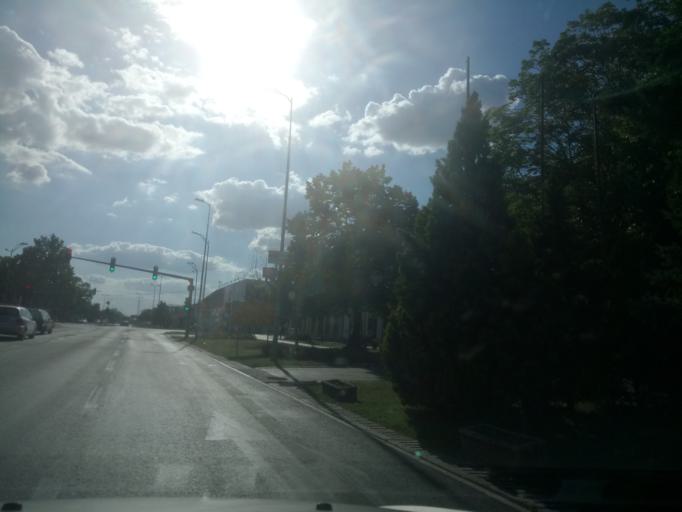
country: RS
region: Autonomna Pokrajina Vojvodina
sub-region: Sremski Okrug
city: Stara Pazova
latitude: 44.9867
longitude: 20.1610
